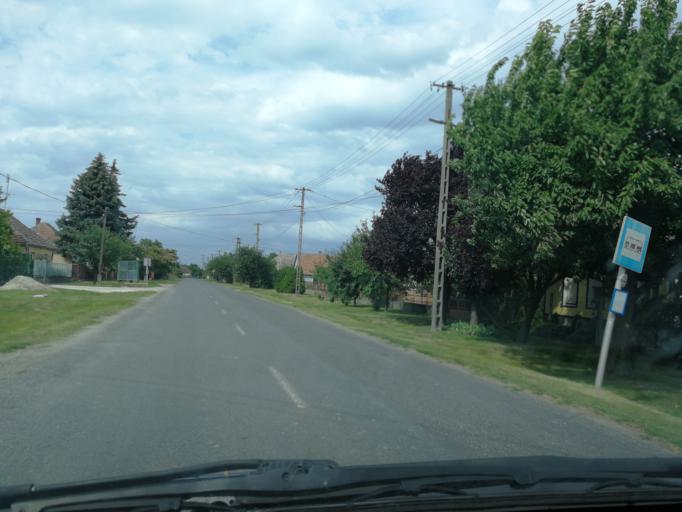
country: HU
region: Bacs-Kiskun
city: Kalocsa
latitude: 46.4629
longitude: 19.0374
